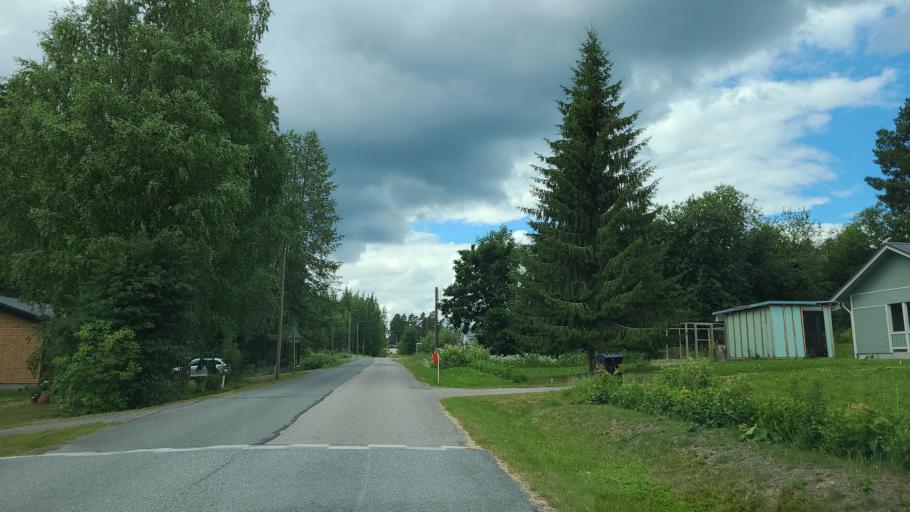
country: FI
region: Northern Savo
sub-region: Koillis-Savo
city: Kaavi
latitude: 62.9725
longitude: 28.4800
